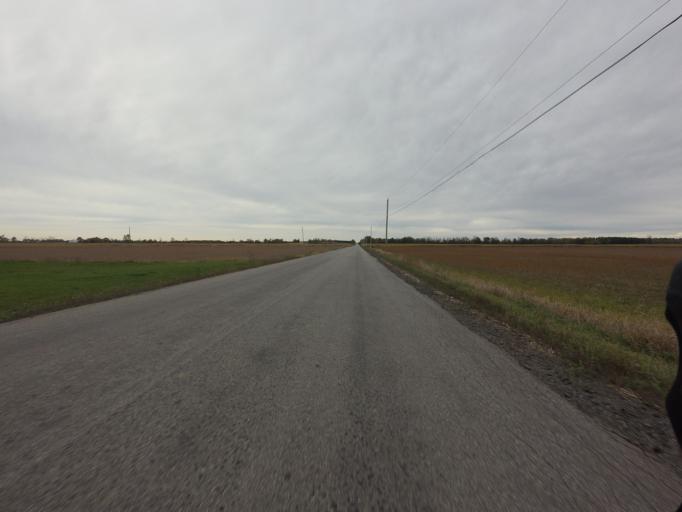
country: CA
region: Ontario
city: Bells Corners
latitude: 45.0969
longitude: -75.7485
